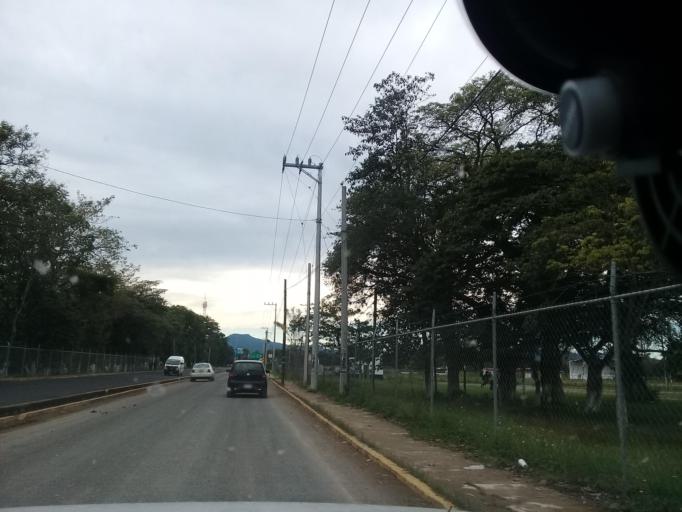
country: MX
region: Hidalgo
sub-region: Huejutla de Reyes
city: Parque de Poblamiento Solidaridad
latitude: 21.1544
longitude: -98.3837
